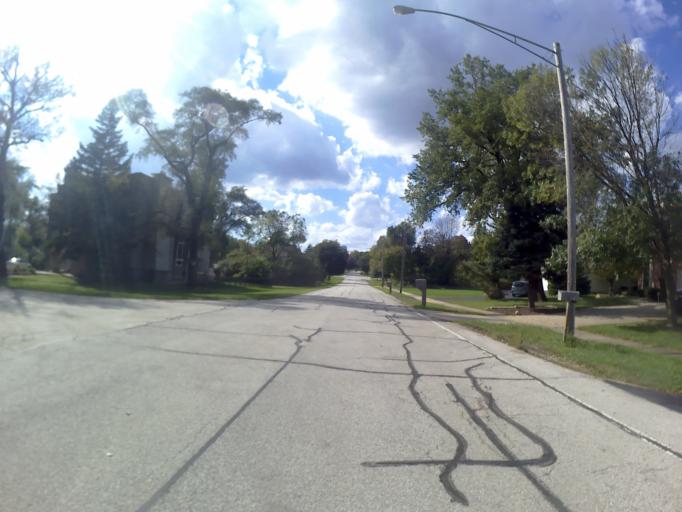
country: US
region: Illinois
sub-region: DuPage County
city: Lisle
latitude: 41.8045
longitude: -88.0894
